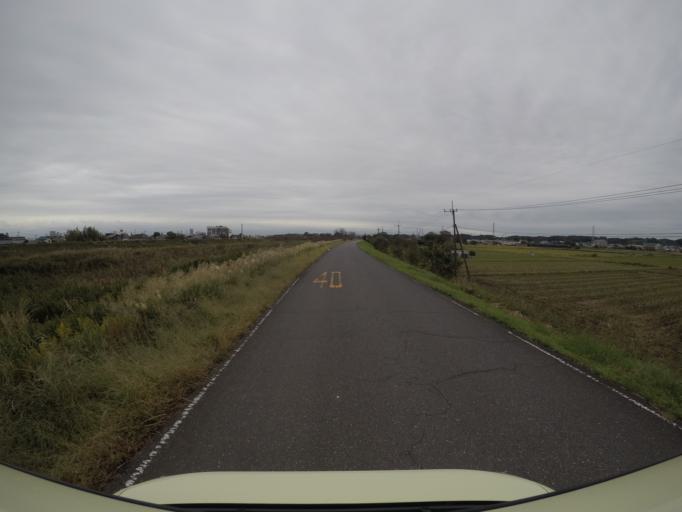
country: JP
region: Ibaraki
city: Naka
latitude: 36.0934
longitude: 140.1712
